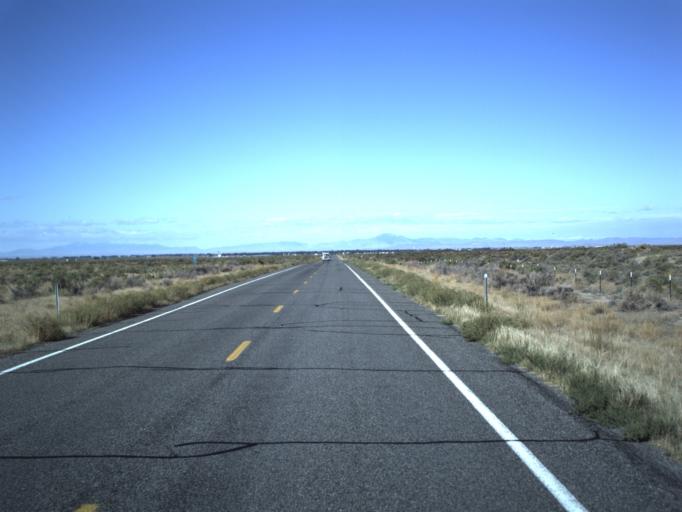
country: US
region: Utah
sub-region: Millard County
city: Delta
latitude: 39.3534
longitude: -112.4770
